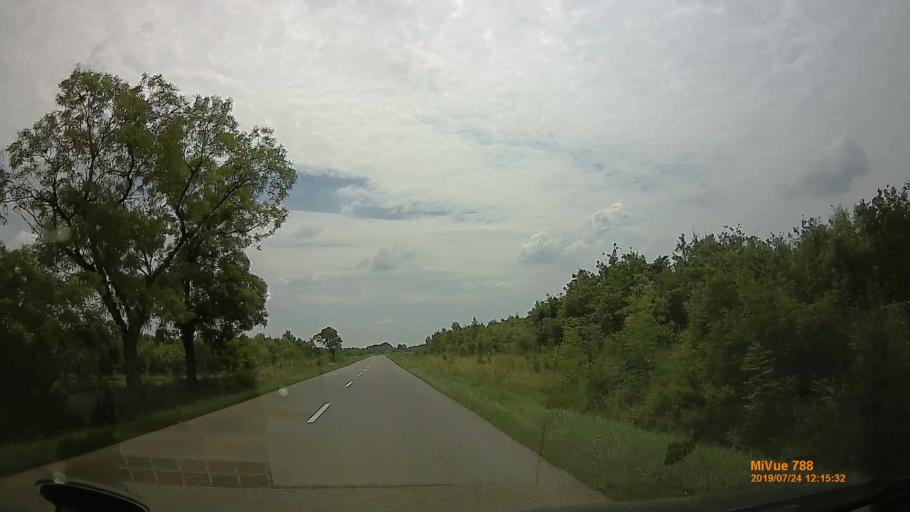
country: HU
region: Szabolcs-Szatmar-Bereg
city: Vasarosnameny
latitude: 48.1831
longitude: 22.3455
